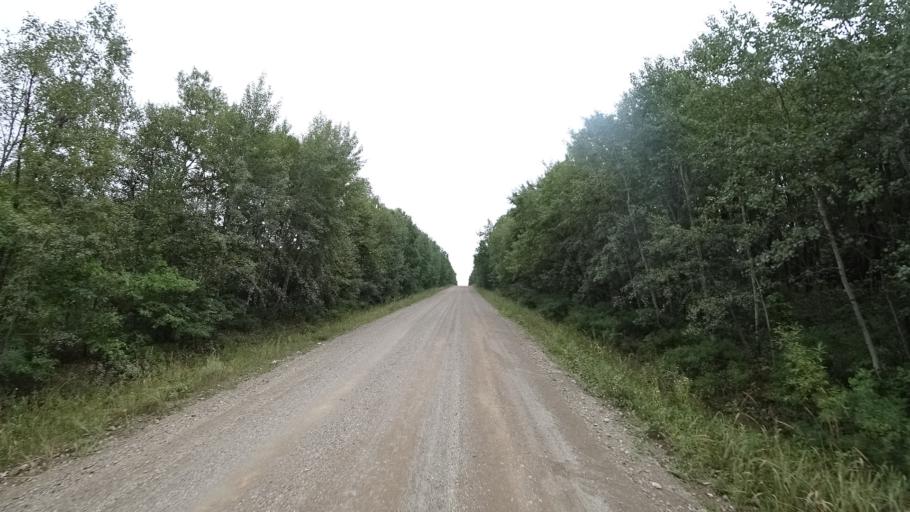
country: RU
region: Primorskiy
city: Ivanovka
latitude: 44.0253
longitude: 132.5170
